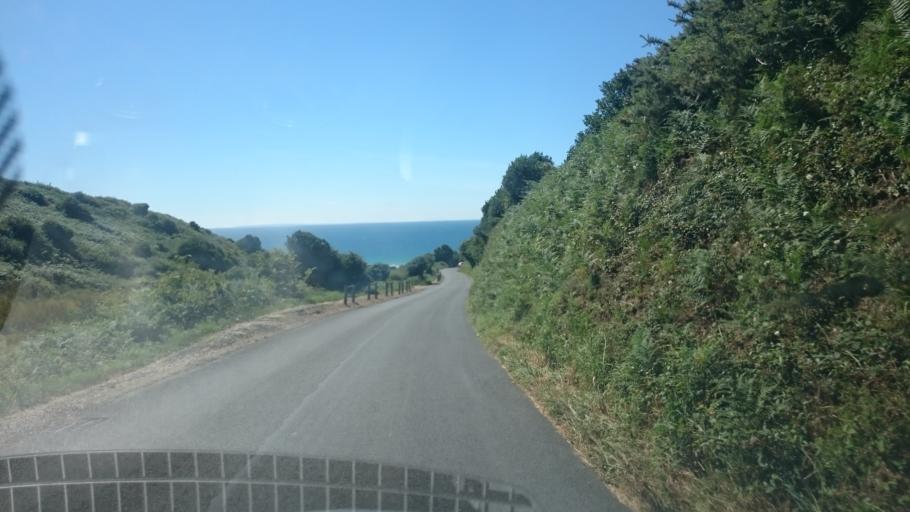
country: FR
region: Lower Normandy
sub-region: Departement de la Manche
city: Les Pieux
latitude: 49.5072
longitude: -1.8407
